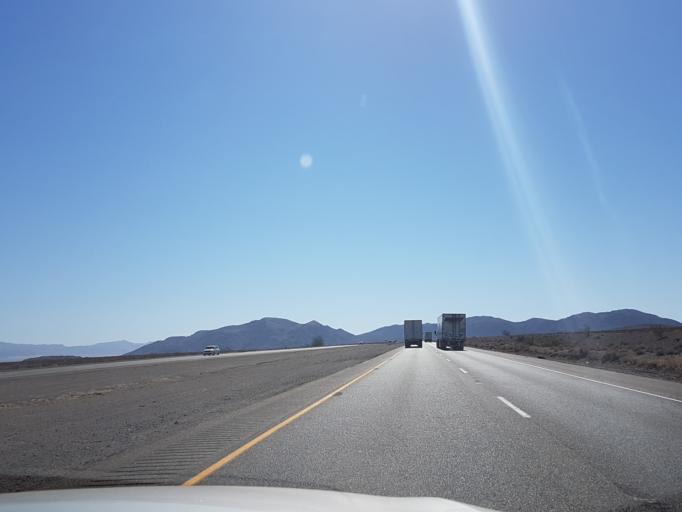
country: US
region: California
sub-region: San Bernardino County
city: Fort Irwin
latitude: 35.2312
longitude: -116.1029
